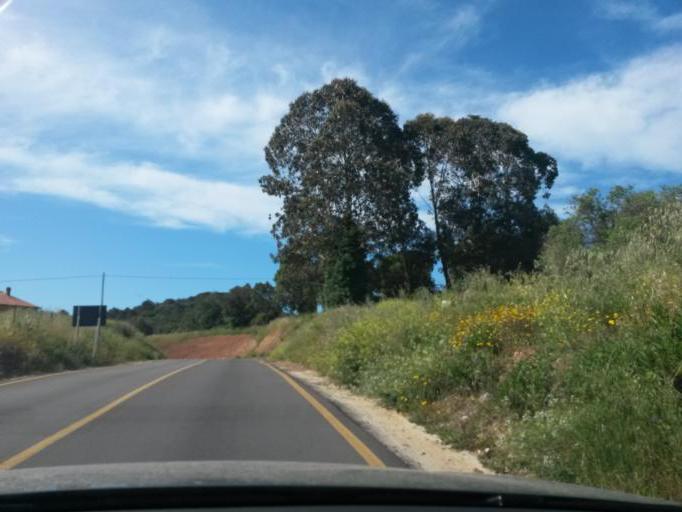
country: IT
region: Tuscany
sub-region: Provincia di Livorno
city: Rio nell'Elba
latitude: 42.8120
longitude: 10.4119
